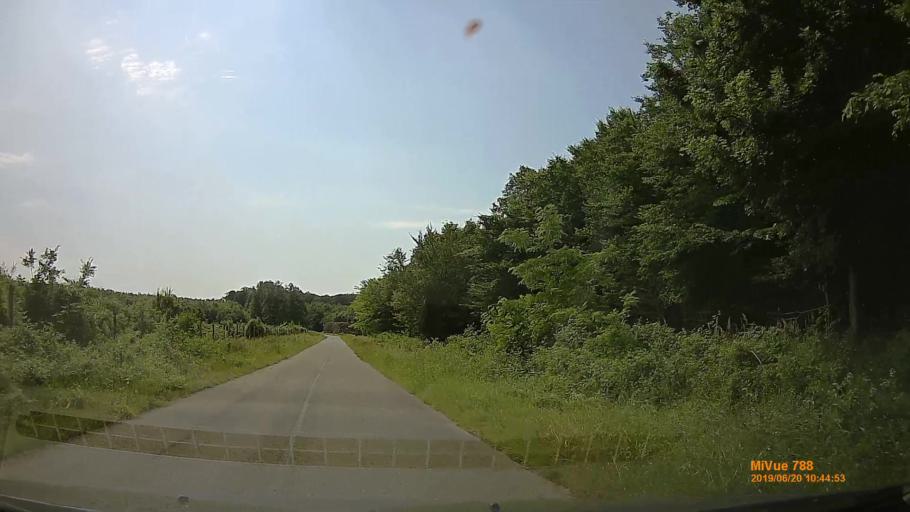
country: HU
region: Baranya
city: Hidas
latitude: 46.1859
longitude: 18.5681
